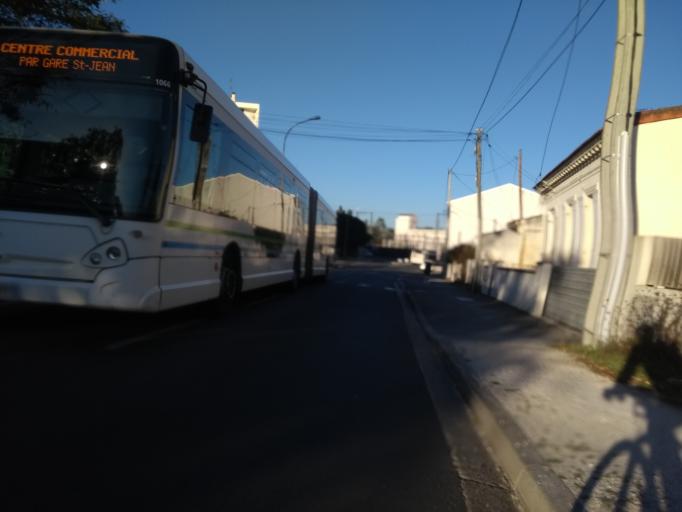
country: FR
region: Aquitaine
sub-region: Departement de la Gironde
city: Talence
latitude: 44.7960
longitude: -0.6078
